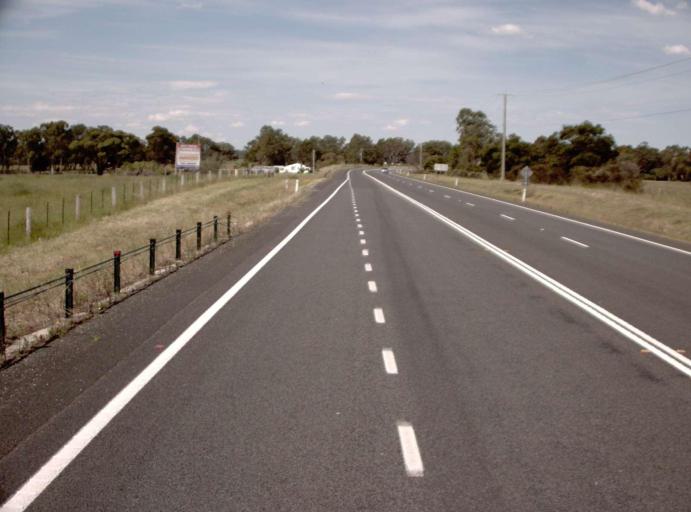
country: AU
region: Victoria
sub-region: East Gippsland
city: Lakes Entrance
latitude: -37.8202
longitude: 147.8103
